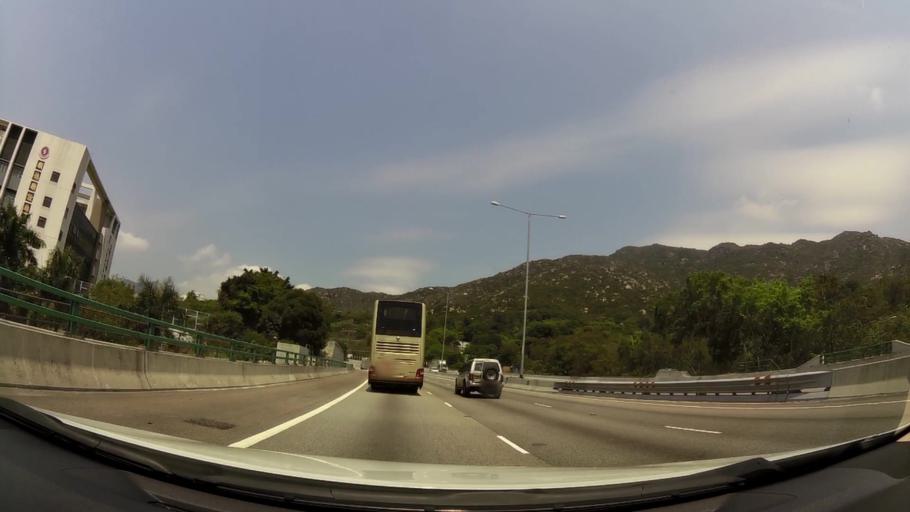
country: HK
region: Tuen Mun
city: Tuen Mun
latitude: 22.3746
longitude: 113.9967
